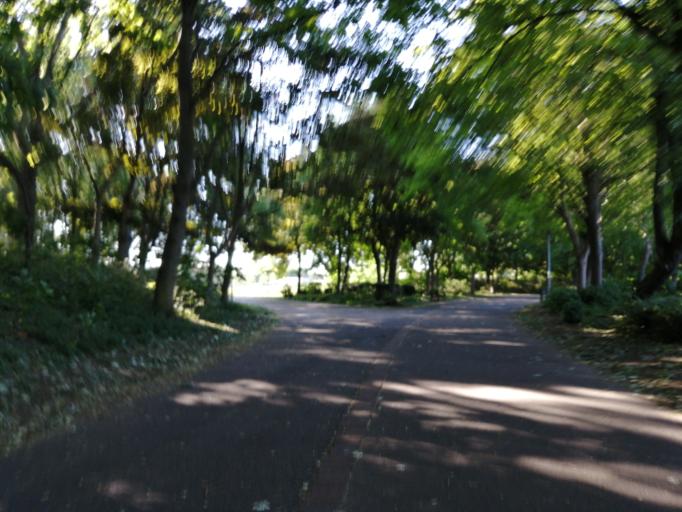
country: GB
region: England
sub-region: Peterborough
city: Marholm
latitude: 52.5987
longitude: -0.2792
